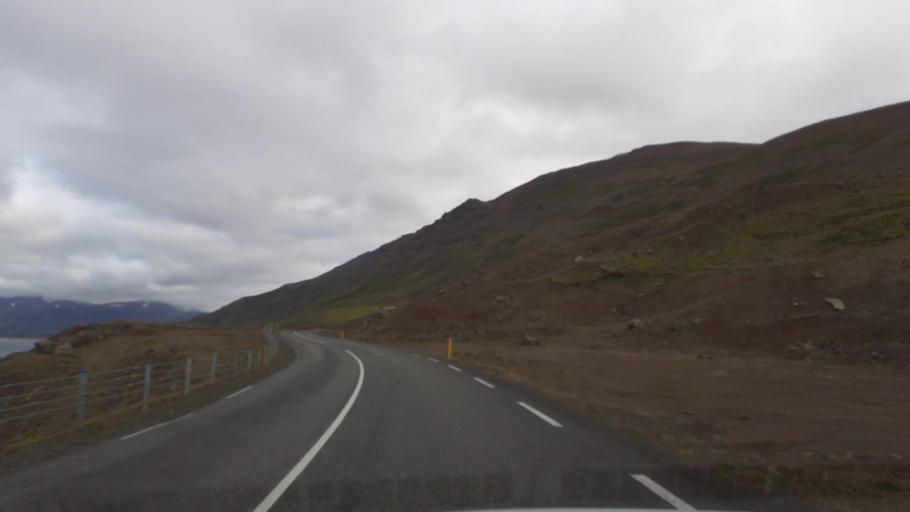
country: IS
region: Northeast
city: Akureyri
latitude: 65.8329
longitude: -18.0564
